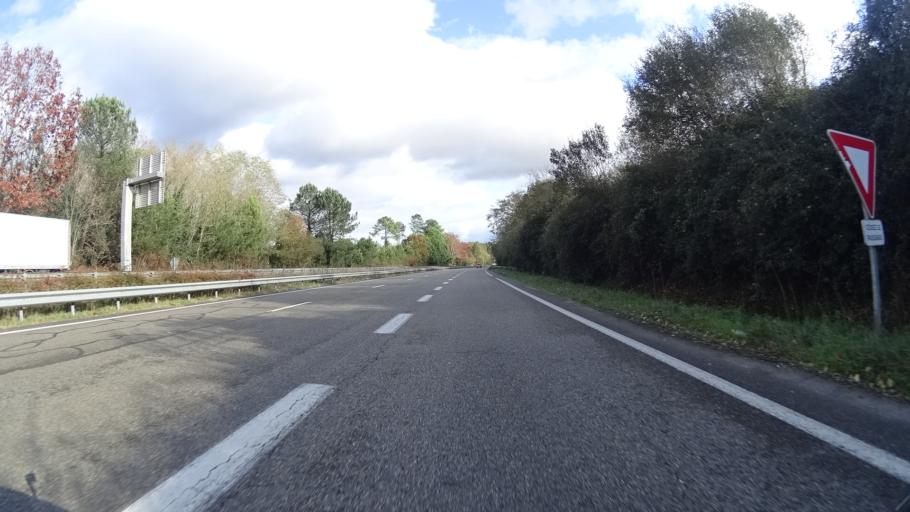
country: FR
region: Aquitaine
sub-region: Departement des Landes
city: Saint-Paul-les-Dax
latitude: 43.7445
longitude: -1.0528
